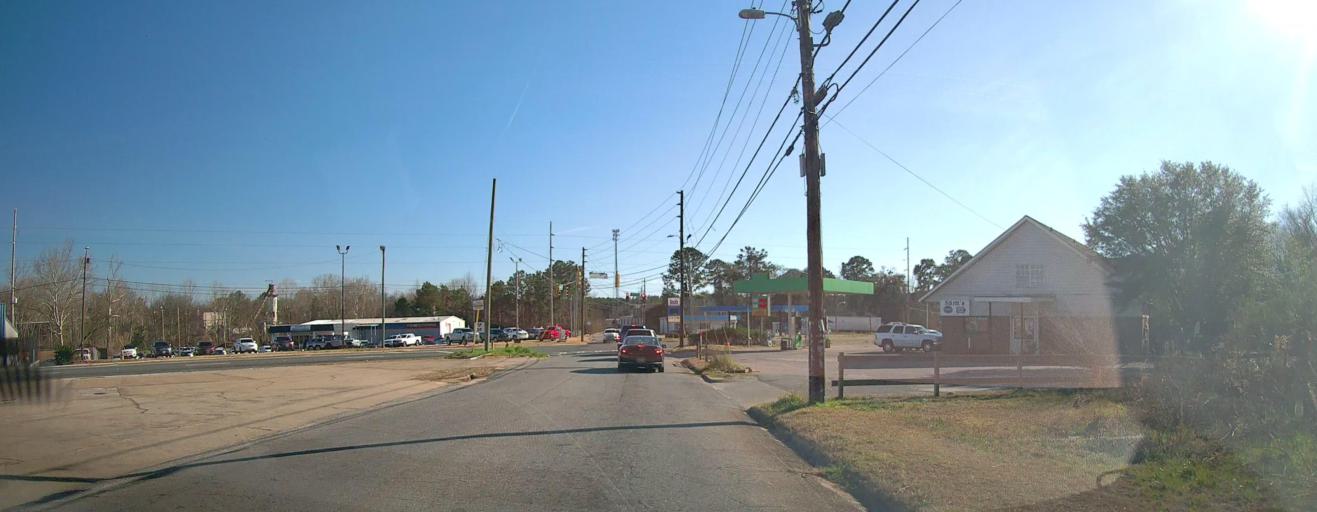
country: US
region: Georgia
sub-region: Sumter County
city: Americus
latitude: 32.0741
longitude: -84.2449
